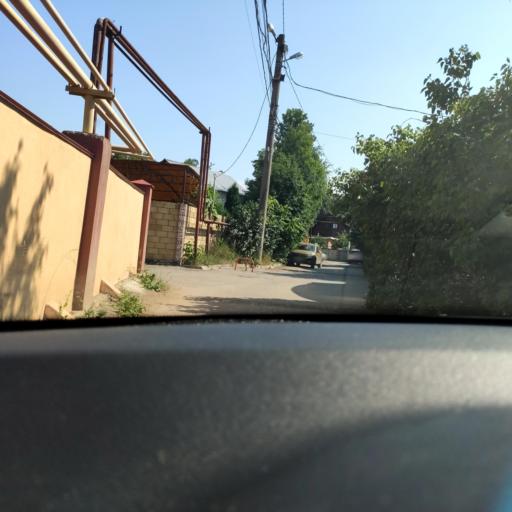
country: RU
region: Samara
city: Samara
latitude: 53.2869
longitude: 50.1949
